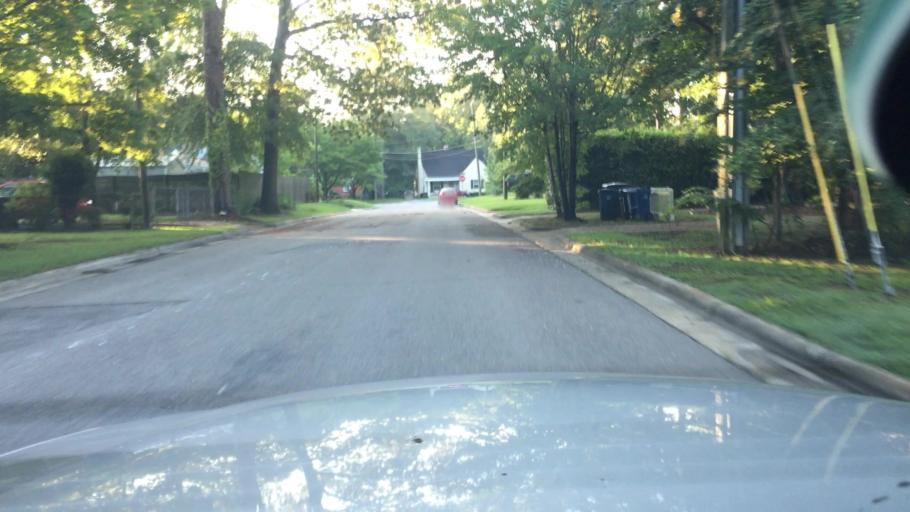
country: US
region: North Carolina
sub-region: Cumberland County
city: Fayetteville
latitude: 35.0618
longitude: -78.9121
